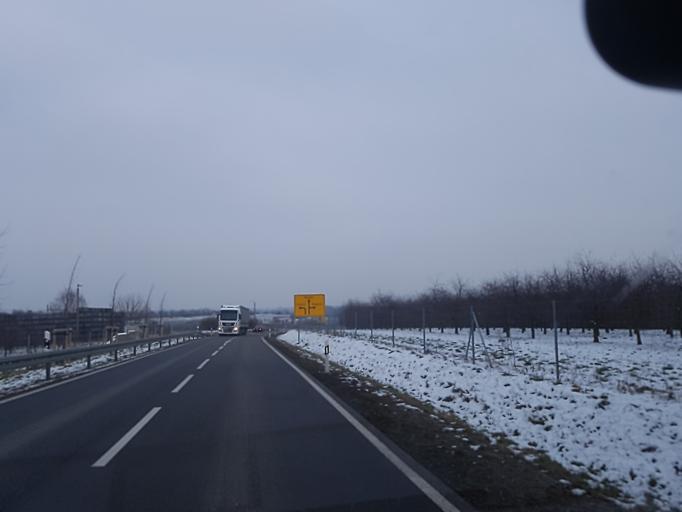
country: DE
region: Saxony
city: Mugeln
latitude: 51.2267
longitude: 13.0126
